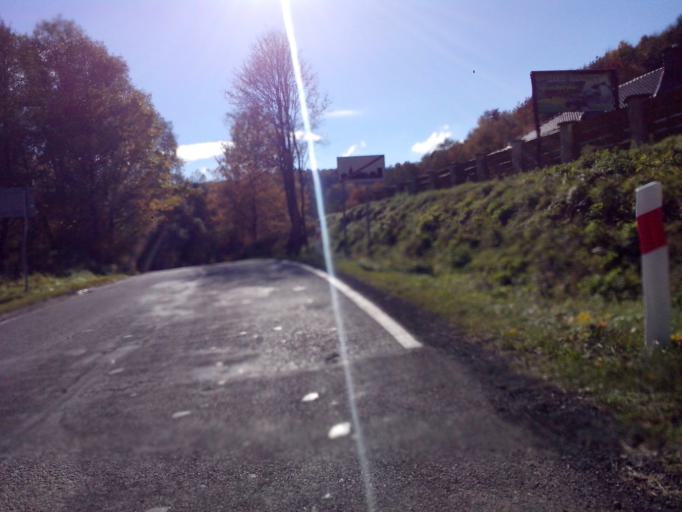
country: PL
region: Subcarpathian Voivodeship
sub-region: Powiat krosnienski
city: Korczyna
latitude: 49.7709
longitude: 21.8487
